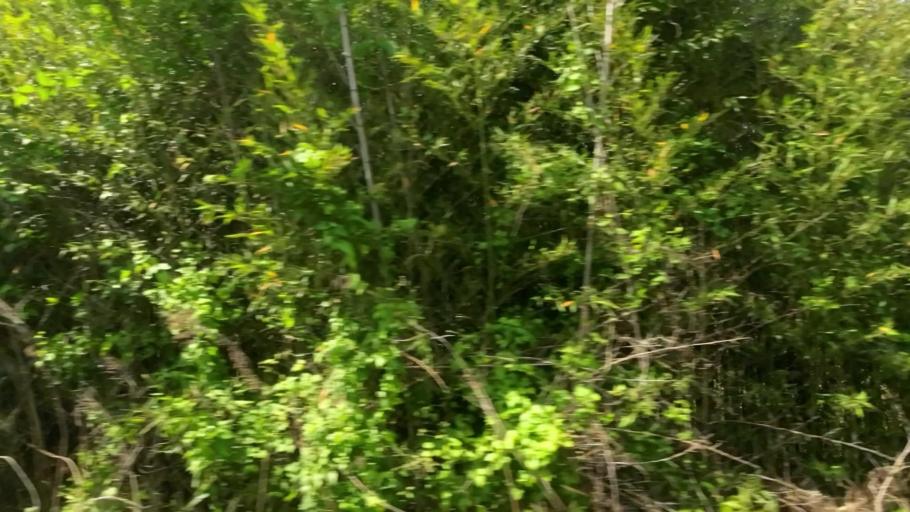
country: JP
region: Tokushima
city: Wakimachi
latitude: 34.0575
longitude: 134.2212
